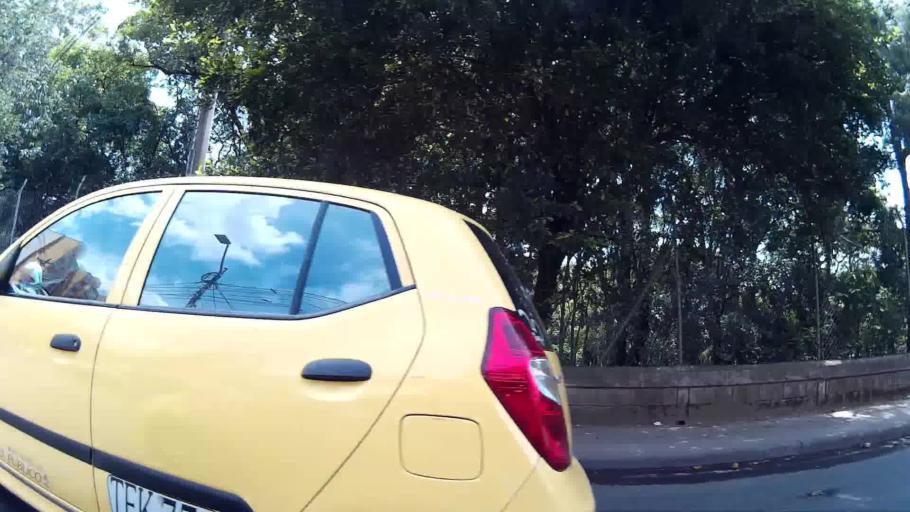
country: CO
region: Antioquia
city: Medellin
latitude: 6.2568
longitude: -75.6258
